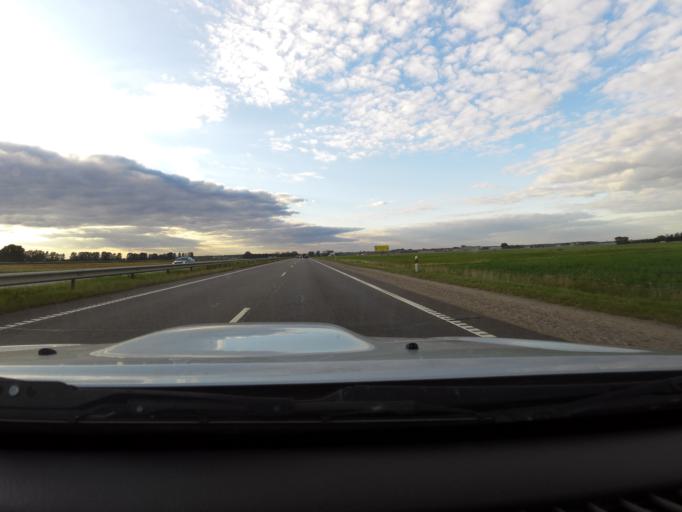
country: LT
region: Kauno apskritis
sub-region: Kauno rajonas
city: Akademija (Kaunas)
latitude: 54.8694
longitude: 23.8285
